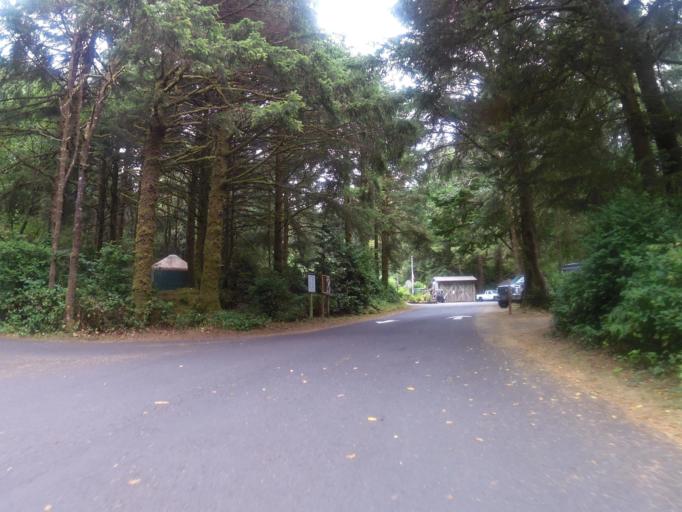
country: US
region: Oregon
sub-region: Lane County
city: Florence
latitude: 44.1607
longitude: -124.1128
